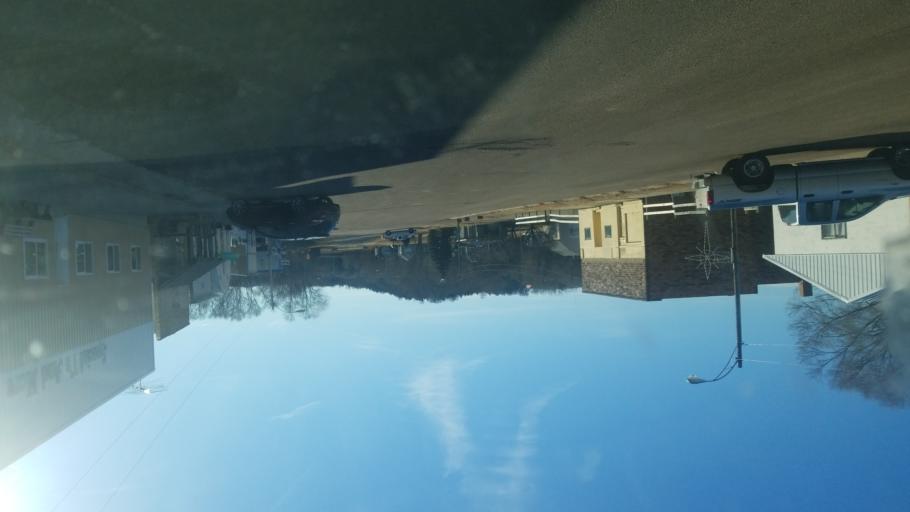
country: US
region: South Dakota
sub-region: Charles Mix County
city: Wagner
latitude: 42.8302
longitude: -98.4663
